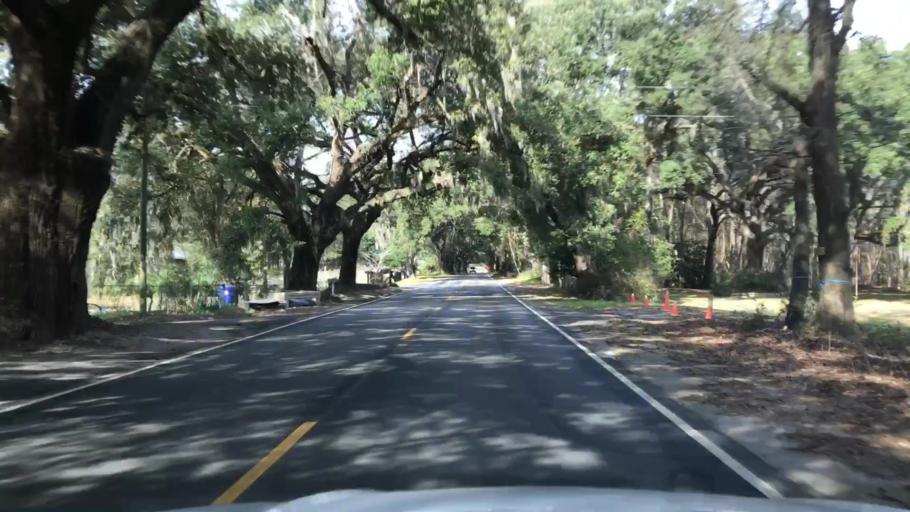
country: US
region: South Carolina
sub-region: Charleston County
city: Shell Point
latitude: 32.7366
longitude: -80.0331
